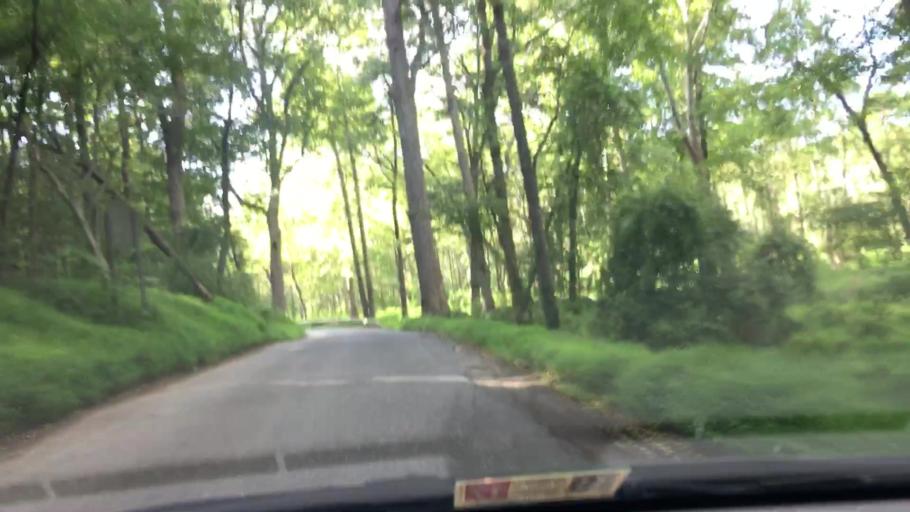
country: US
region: Maryland
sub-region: Montgomery County
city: Montgomery Village
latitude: 39.2129
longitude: -77.2052
